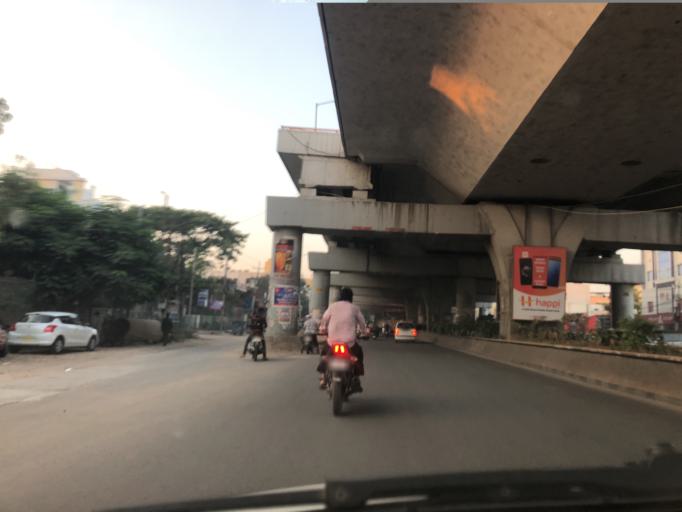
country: IN
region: Telangana
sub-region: Hyderabad
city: Hyderabad
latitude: 17.3810
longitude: 78.4294
